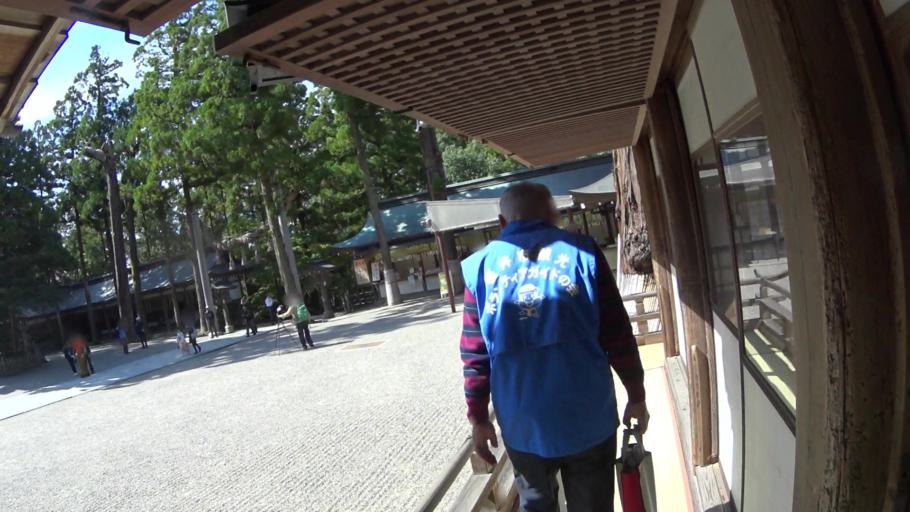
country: JP
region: Nara
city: Sakurai
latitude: 34.5291
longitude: 135.8530
